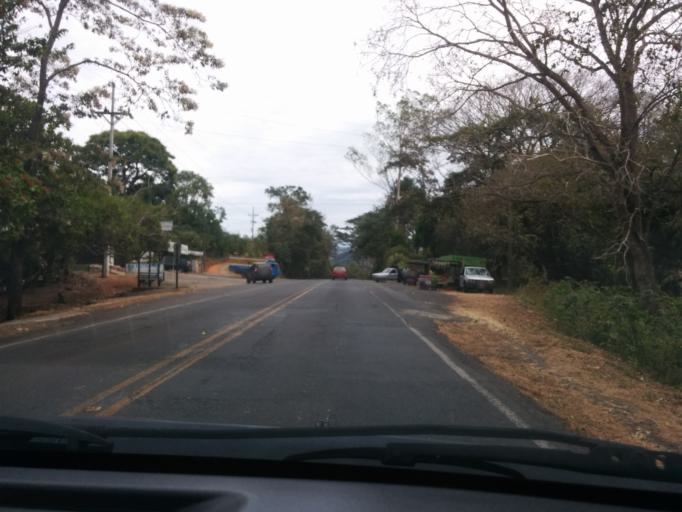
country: CR
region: Puntarenas
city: Esparza
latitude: 10.0020
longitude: -84.6409
